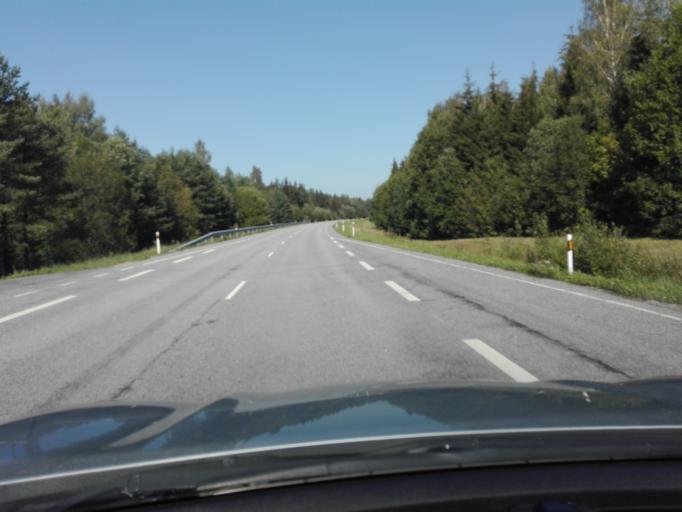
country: EE
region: Raplamaa
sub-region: Rapla vald
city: Rapla
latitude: 59.0046
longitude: 24.7689
